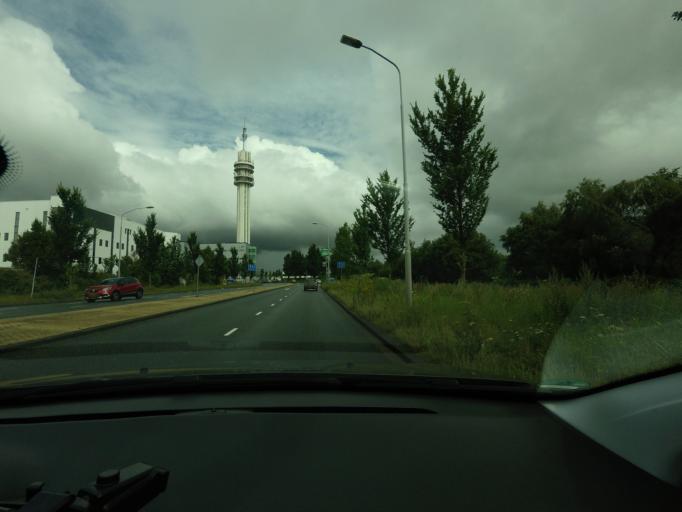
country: NL
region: North Holland
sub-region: Gemeente Haarlem
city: Haarlem
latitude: 52.3863
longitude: 4.6719
